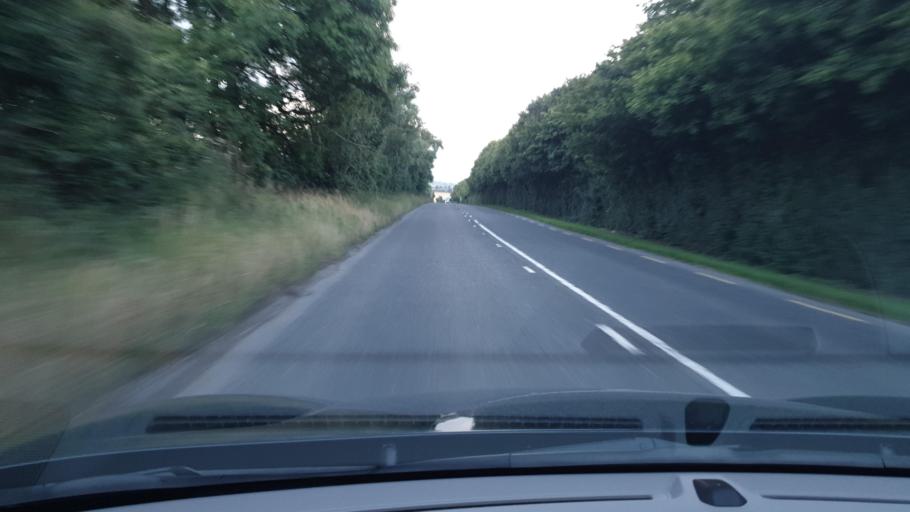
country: IE
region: Leinster
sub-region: Lu
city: Drogheda
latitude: 53.6867
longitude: -6.3798
